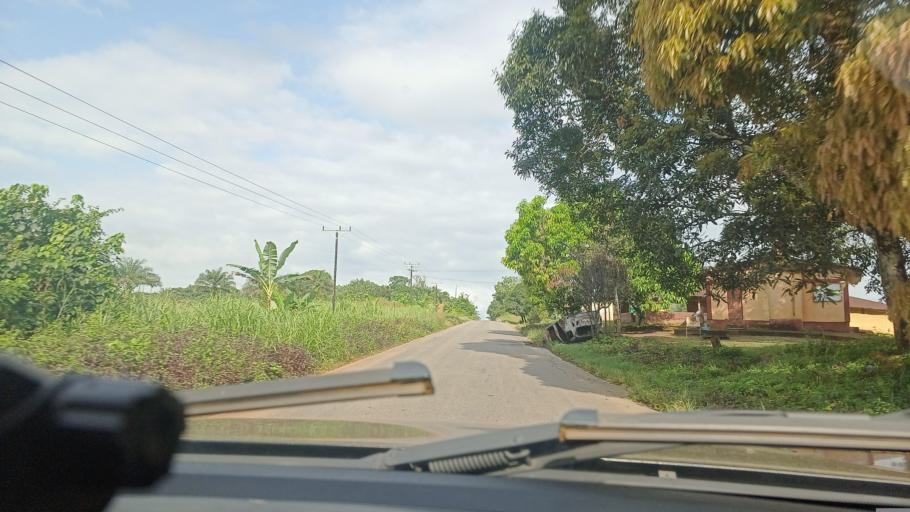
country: LR
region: Bomi
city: Tubmanburg
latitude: 6.7080
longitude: -10.9288
